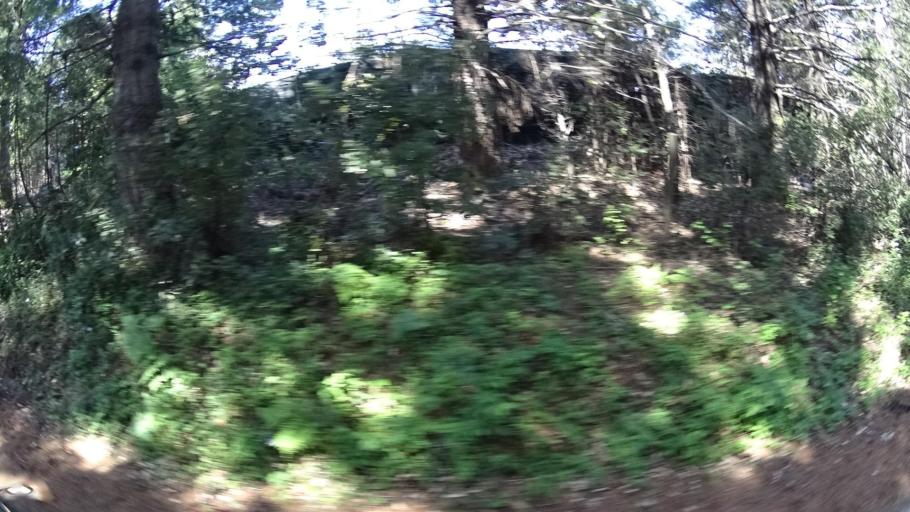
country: US
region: California
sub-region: Humboldt County
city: Redway
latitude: 40.1784
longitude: -124.0890
